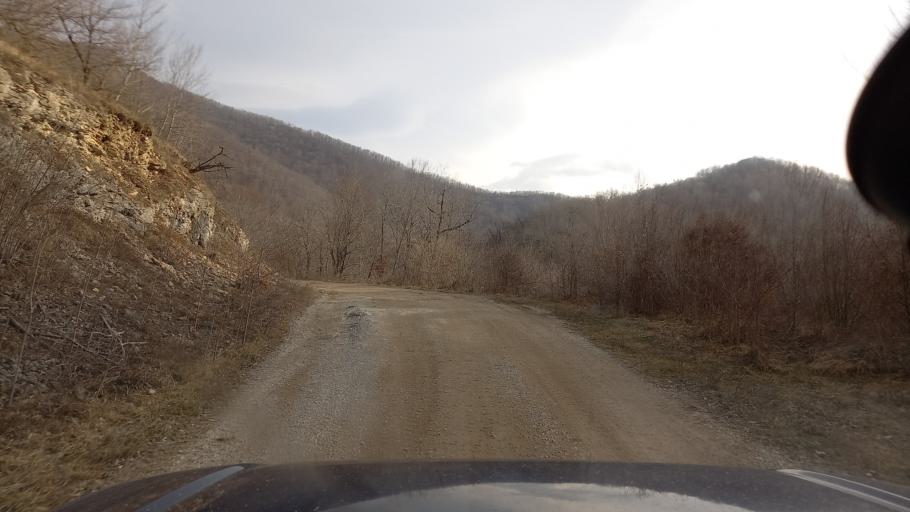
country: RU
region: Adygeya
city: Kamennomostskiy
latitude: 44.1499
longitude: 40.2974
